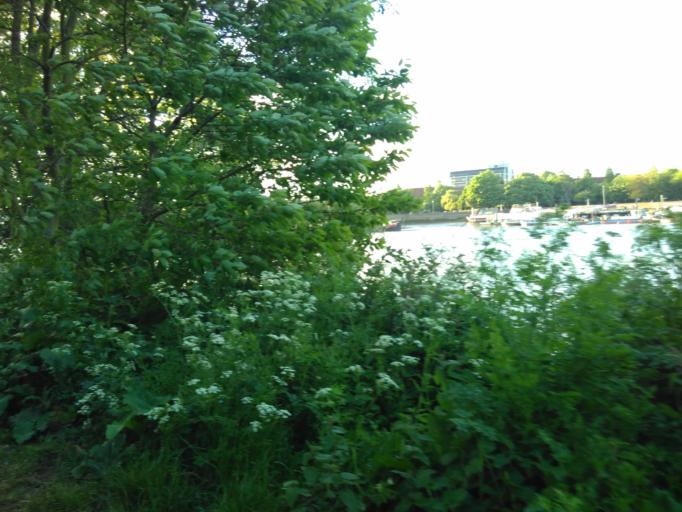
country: GB
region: England
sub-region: Greater London
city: Hammersmith
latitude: 51.4884
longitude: -0.2327
